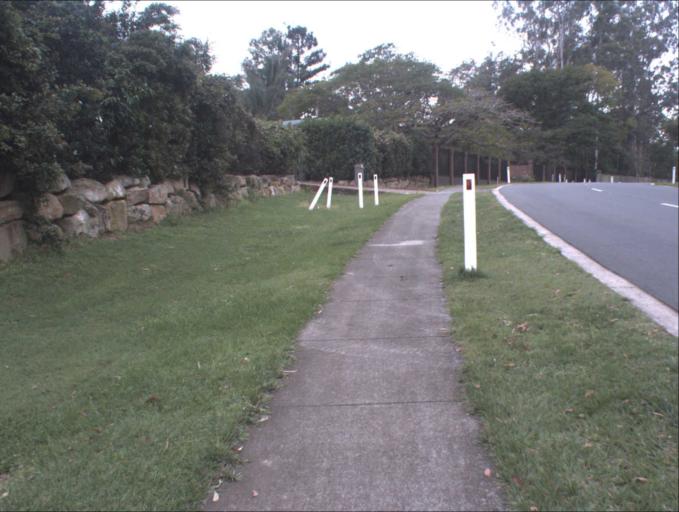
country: AU
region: Queensland
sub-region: Brisbane
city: Forest Lake
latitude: -27.6684
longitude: 153.0014
